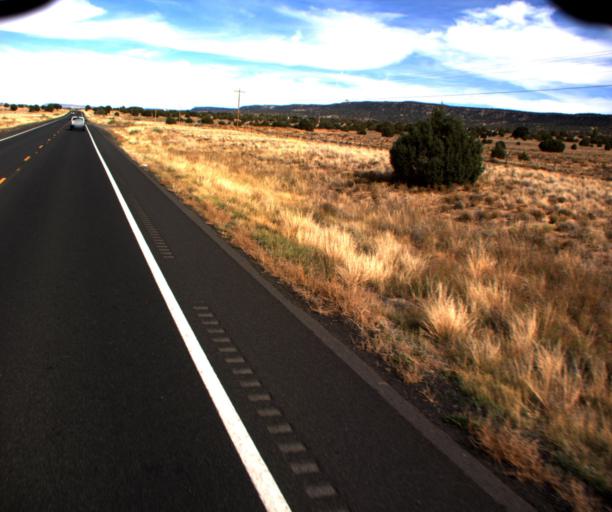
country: US
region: Arizona
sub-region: Coconino County
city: Kaibito
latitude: 36.4867
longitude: -110.6387
